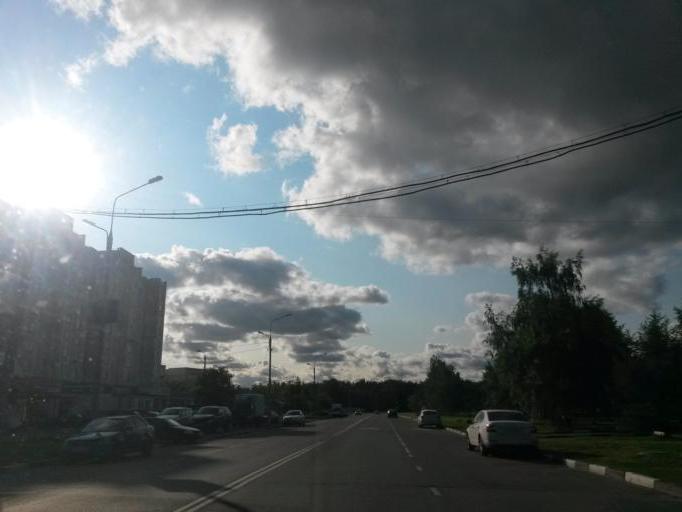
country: RU
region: Moscow
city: Zhulebino
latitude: 55.6868
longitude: 37.8501
